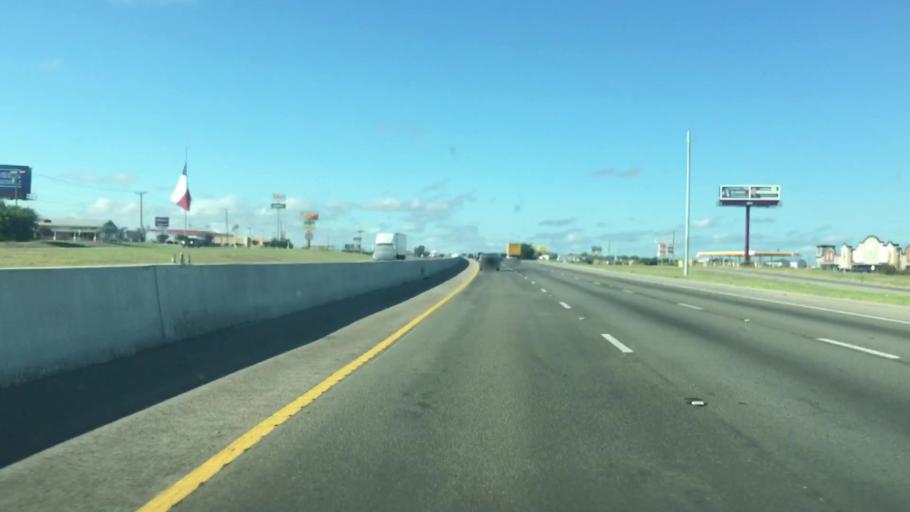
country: US
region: Texas
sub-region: Williamson County
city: Serenada
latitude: 30.8169
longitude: -97.6103
